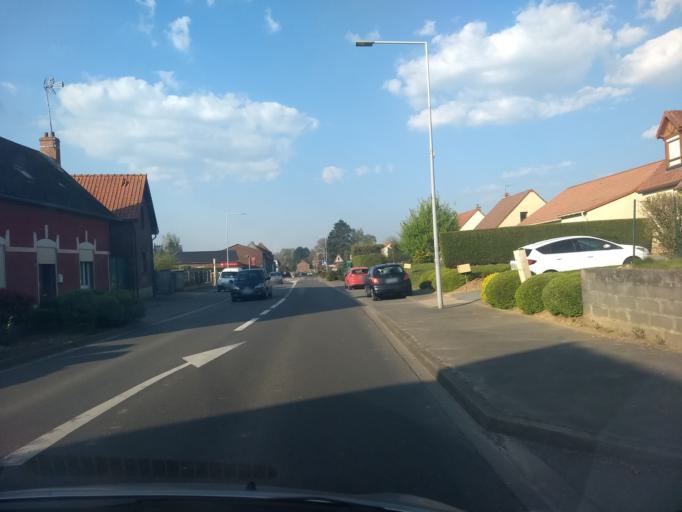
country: FR
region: Nord-Pas-de-Calais
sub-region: Departement du Pas-de-Calais
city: Bucquoy
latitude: 50.1471
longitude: 2.7165
